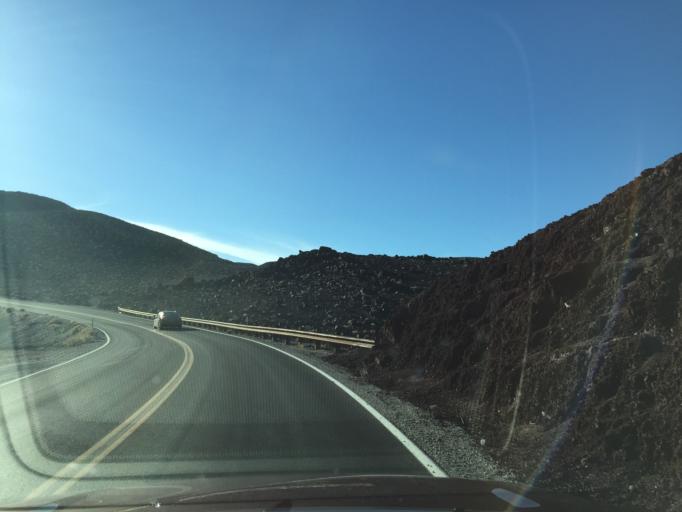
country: US
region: California
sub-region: Inyo County
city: Lone Pine
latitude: 36.3582
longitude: -117.5329
